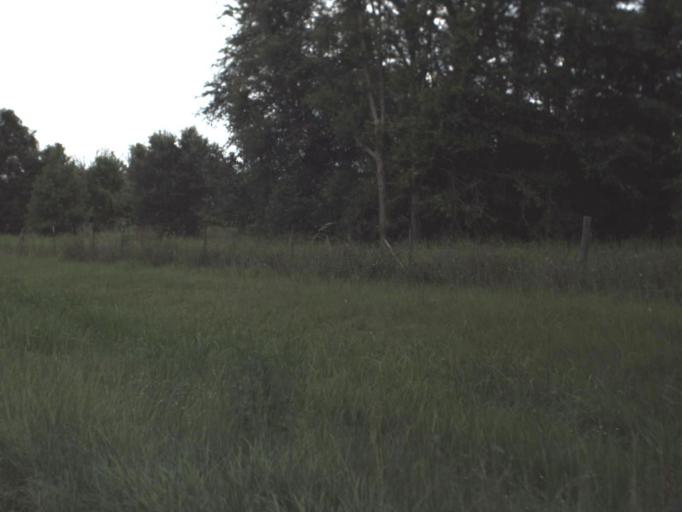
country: US
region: Florida
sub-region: Union County
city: Lake Butler
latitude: 29.8950
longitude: -82.3541
